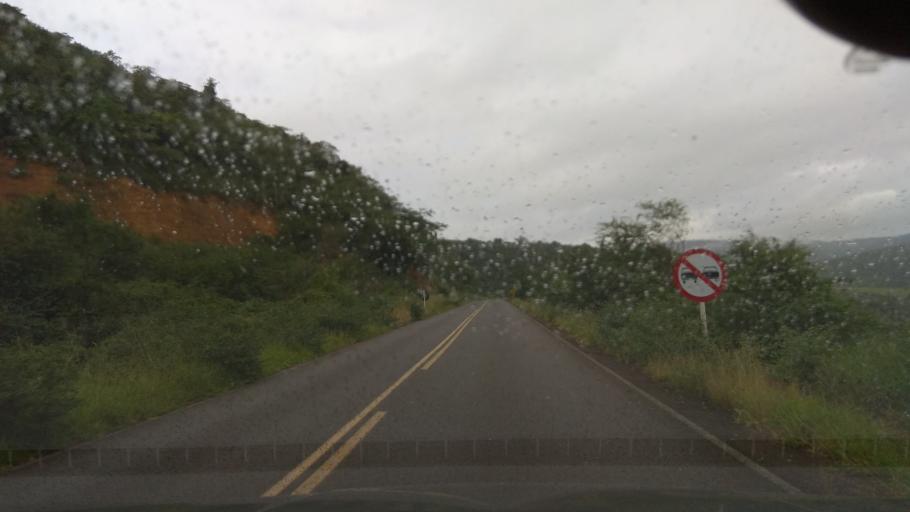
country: BR
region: Bahia
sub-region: Ubaira
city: Ubaira
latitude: -13.2405
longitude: -39.7389
